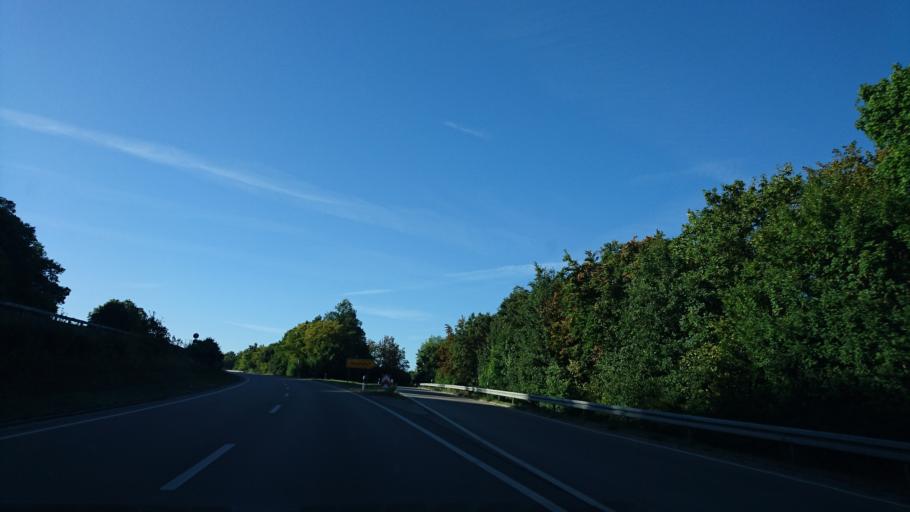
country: DE
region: Bavaria
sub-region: Swabia
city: Donauwoerth
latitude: 48.7320
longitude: 10.7835
